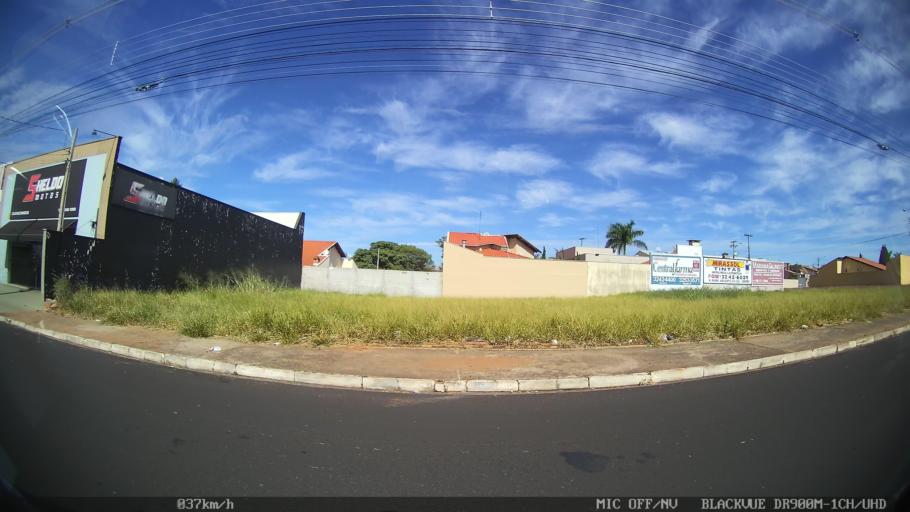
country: BR
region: Sao Paulo
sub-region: Bady Bassitt
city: Bady Bassitt
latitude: -20.8157
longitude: -49.4926
